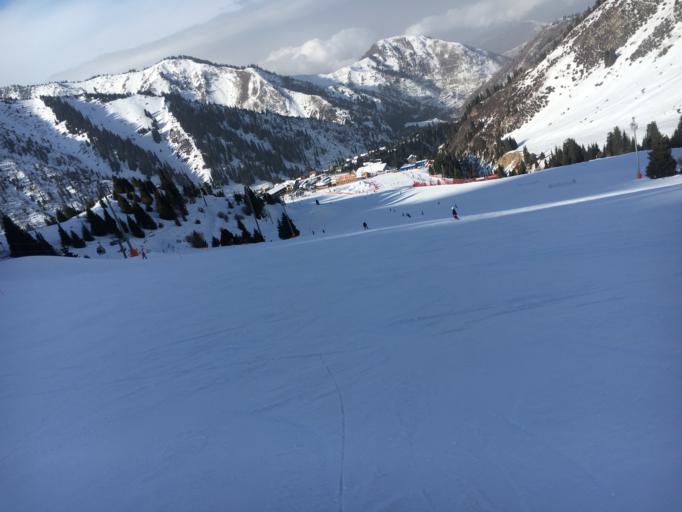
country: KZ
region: Almaty Qalasy
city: Almaty
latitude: 43.1234
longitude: 77.0927
